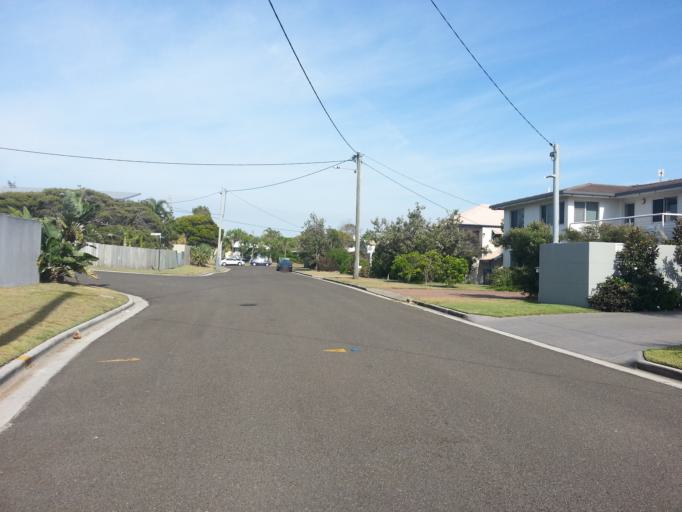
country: AU
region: Queensland
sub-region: Sunshine Coast
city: Peregian Springs
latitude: -26.4927
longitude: 153.0948
